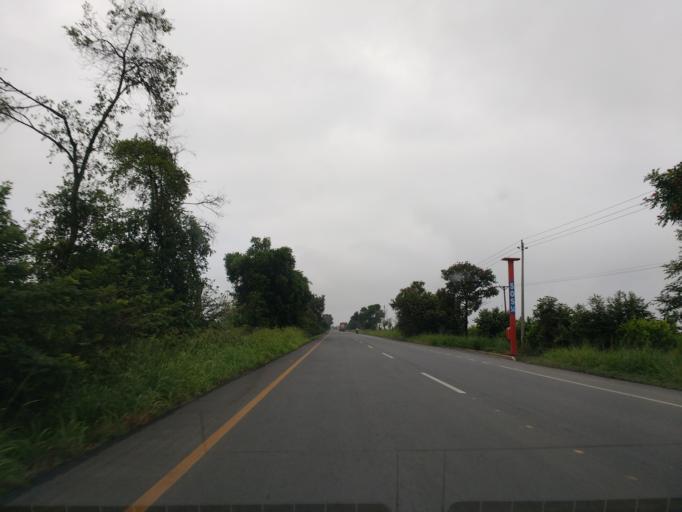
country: CO
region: Valle del Cauca
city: Palmira
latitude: 3.5561
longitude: -76.3361
